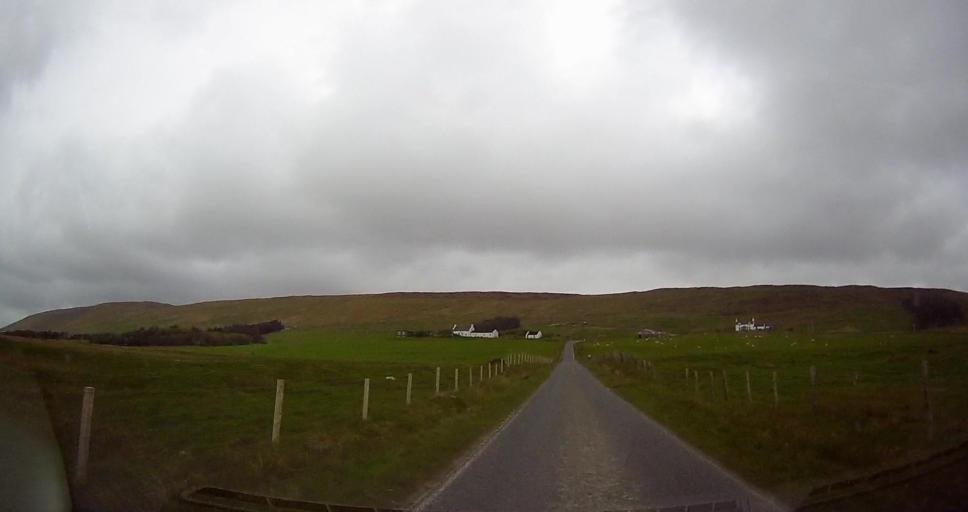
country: GB
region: Scotland
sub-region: Shetland Islands
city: Lerwick
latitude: 60.2751
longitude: -1.2768
